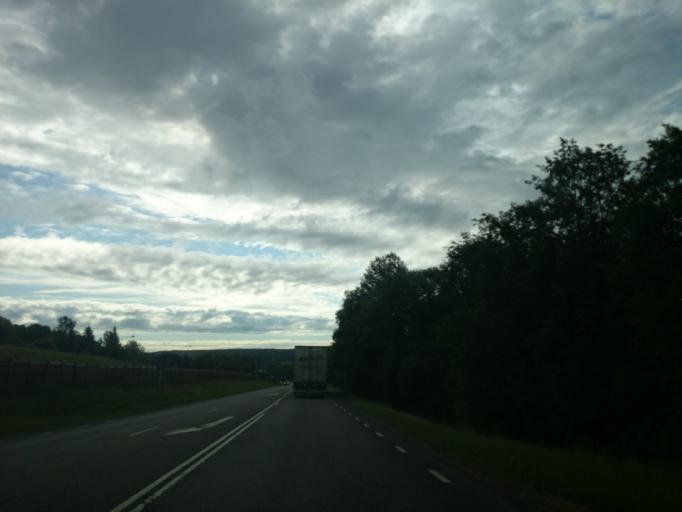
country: SE
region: Vaesternorrland
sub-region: Sundsvalls Kommun
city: Johannedal
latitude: 62.4122
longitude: 17.3723
